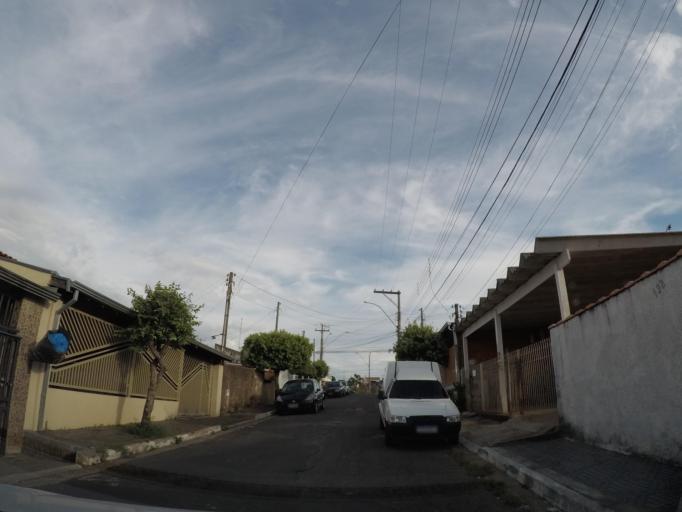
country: BR
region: Sao Paulo
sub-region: Sumare
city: Sumare
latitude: -22.8184
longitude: -47.2544
